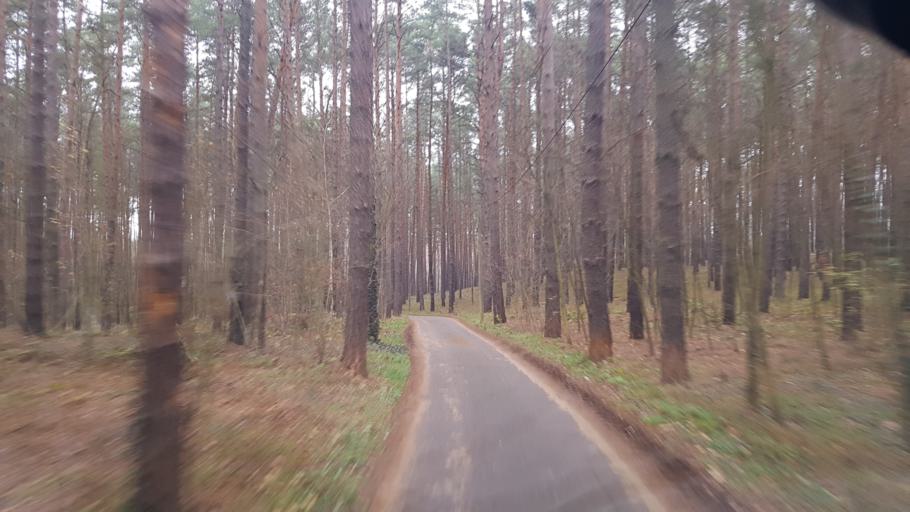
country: DE
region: Brandenburg
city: Schenkendobern
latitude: 51.9696
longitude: 14.6494
